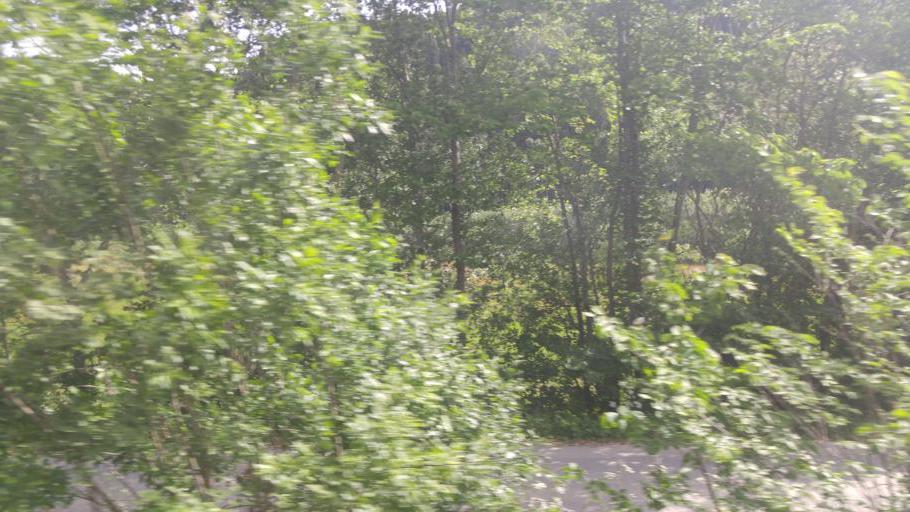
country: NO
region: Sor-Trondelag
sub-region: Midtre Gauldal
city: Storen
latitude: 63.0396
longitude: 10.2956
